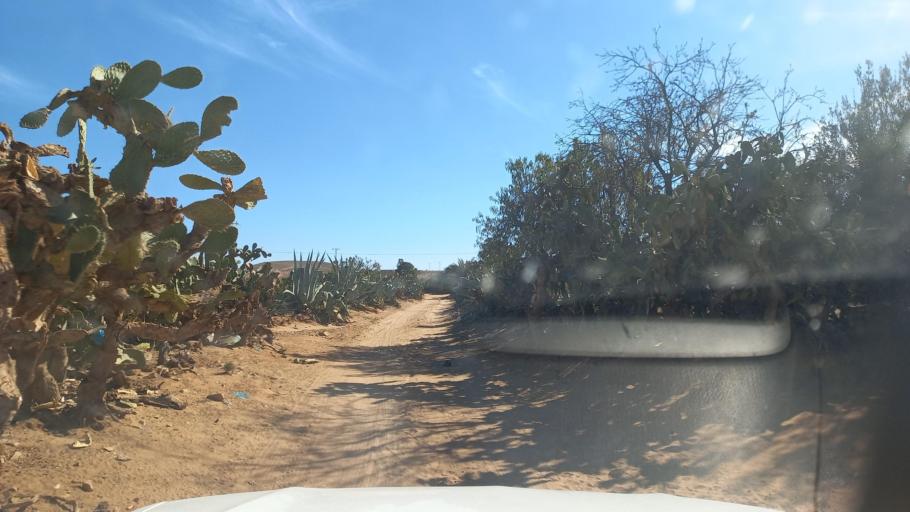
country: TN
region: Al Qasrayn
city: Kasserine
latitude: 35.2102
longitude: 8.9716
